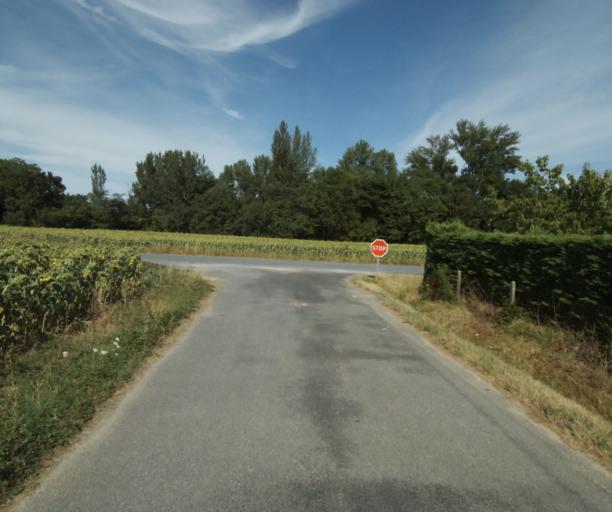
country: FR
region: Midi-Pyrenees
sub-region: Departement du Tarn
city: Soual
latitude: 43.5218
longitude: 2.0700
